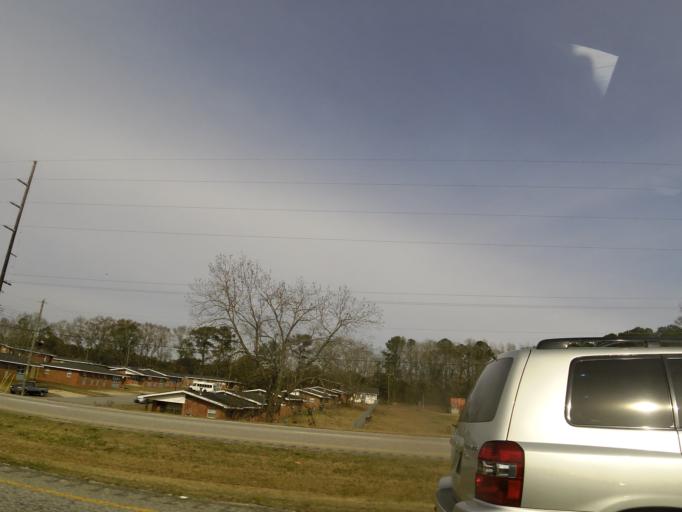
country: US
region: Alabama
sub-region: Dale County
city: Ozark
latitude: 31.4359
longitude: -85.6360
